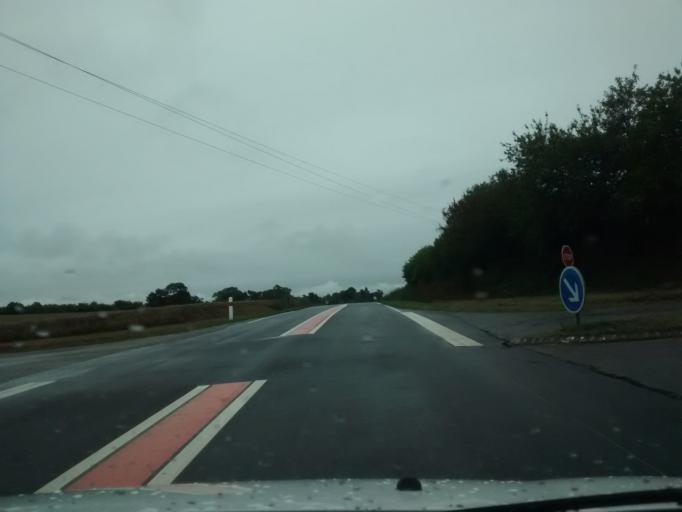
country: FR
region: Brittany
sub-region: Departement d'Ille-et-Vilaine
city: Vern-sur-Seiche
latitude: 48.0482
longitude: -1.5886
